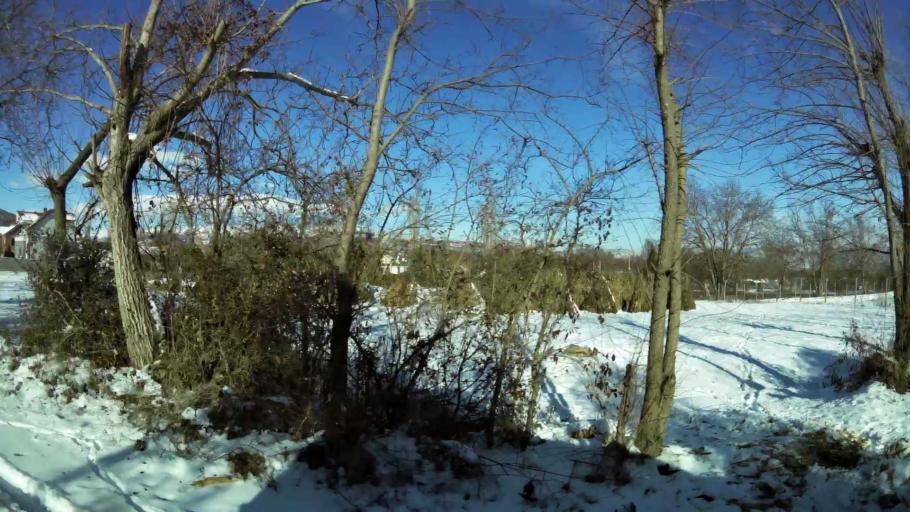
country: MK
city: Grchec
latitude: 41.9783
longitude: 21.3164
